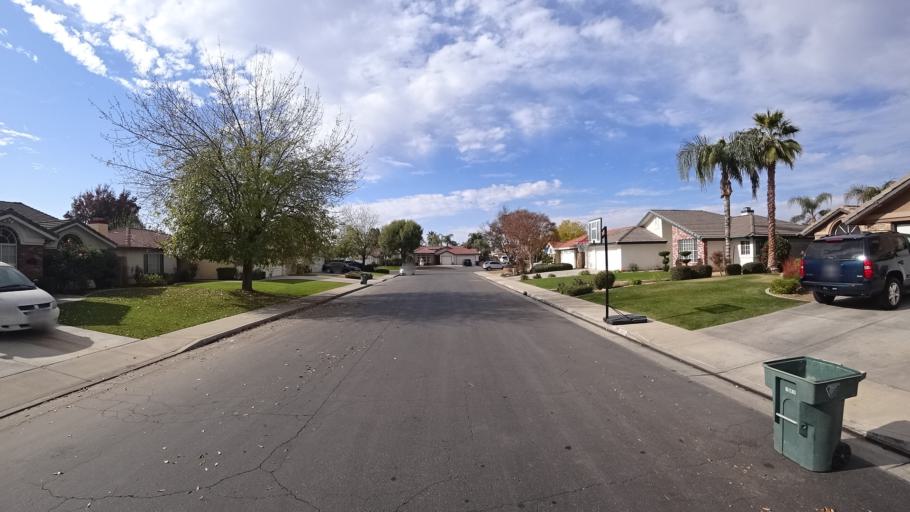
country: US
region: California
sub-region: Kern County
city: Greenacres
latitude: 35.4067
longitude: -119.1221
